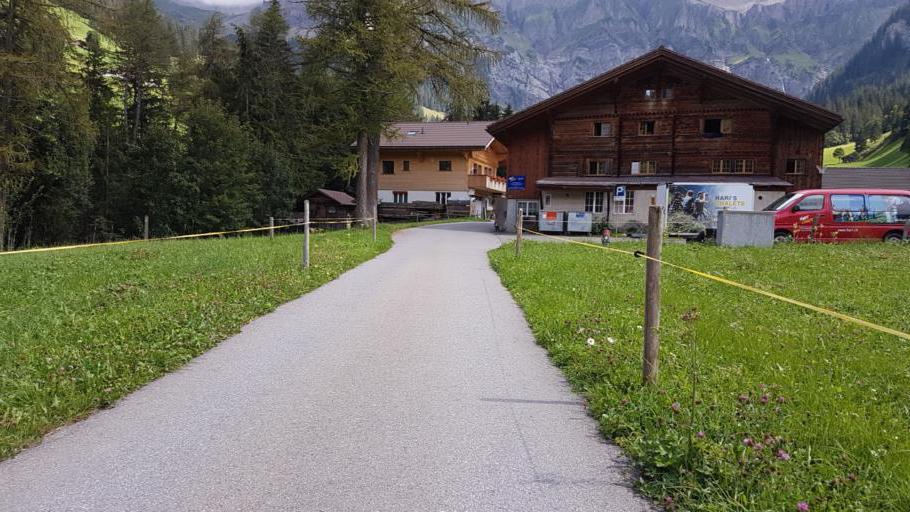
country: CH
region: Bern
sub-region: Frutigen-Niedersimmental District
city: Adelboden
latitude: 46.4915
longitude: 7.5782
